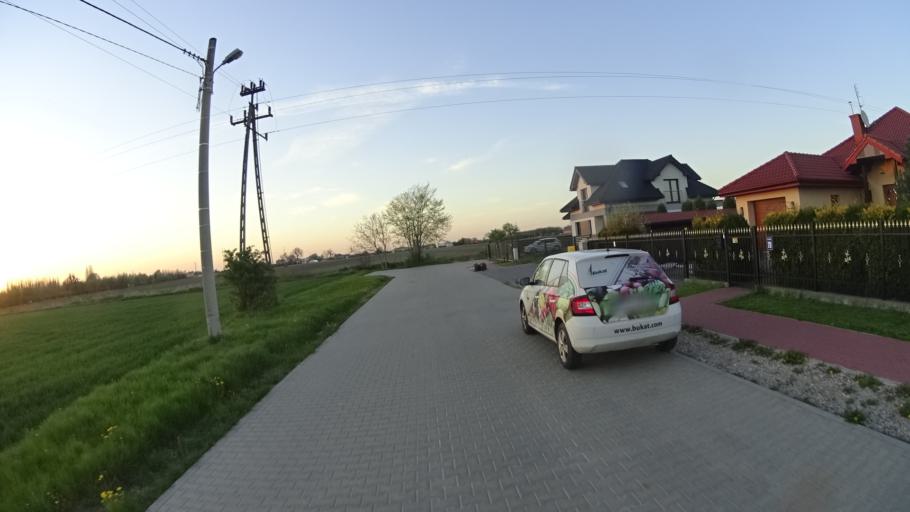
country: PL
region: Masovian Voivodeship
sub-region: Powiat warszawski zachodni
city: Ozarow Mazowiecki
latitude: 52.2225
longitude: 20.7766
